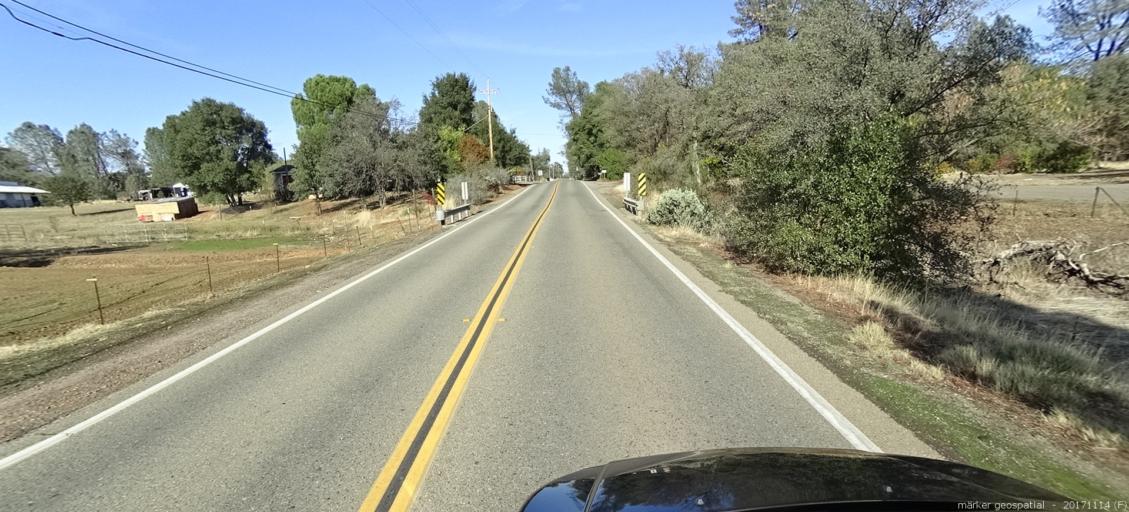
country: US
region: California
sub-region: Shasta County
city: Anderson
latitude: 40.4326
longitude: -122.4075
